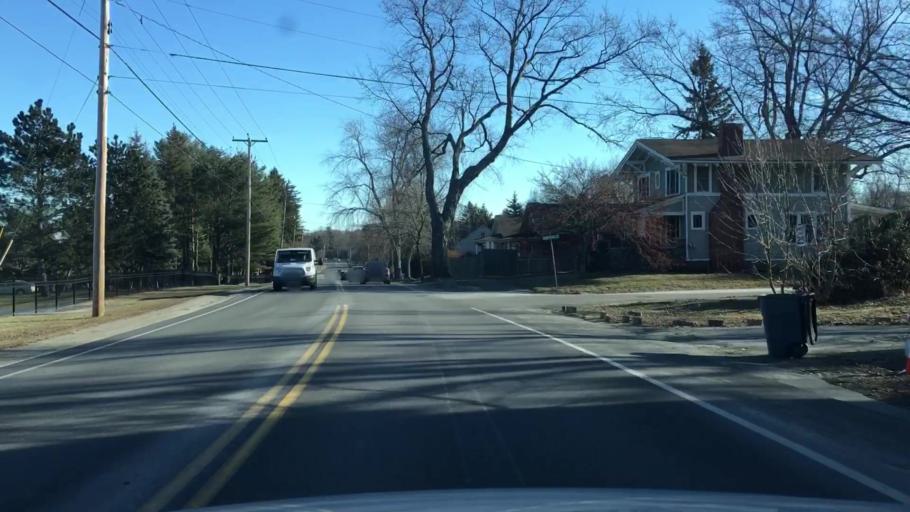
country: US
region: Maine
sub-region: Penobscot County
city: Bangor
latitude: 44.8129
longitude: -68.7947
